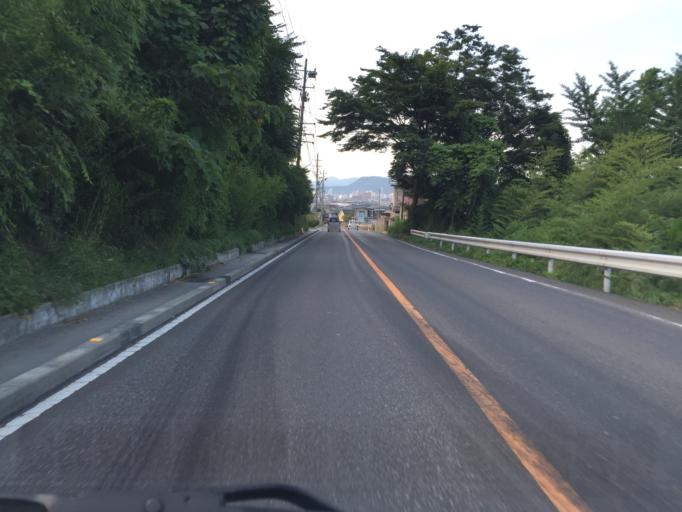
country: JP
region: Fukushima
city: Fukushima-shi
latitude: 37.7190
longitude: 140.4623
